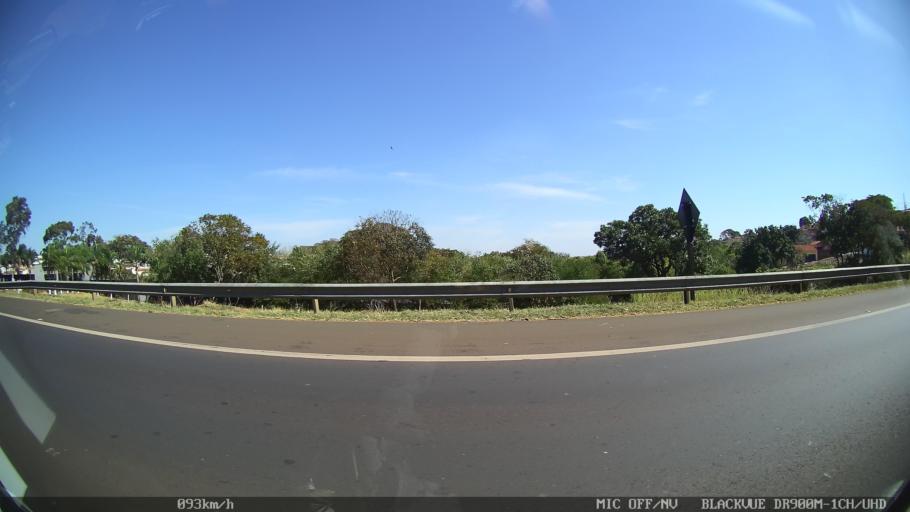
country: BR
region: Sao Paulo
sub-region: Franca
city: Franca
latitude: -20.5343
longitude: -47.4245
